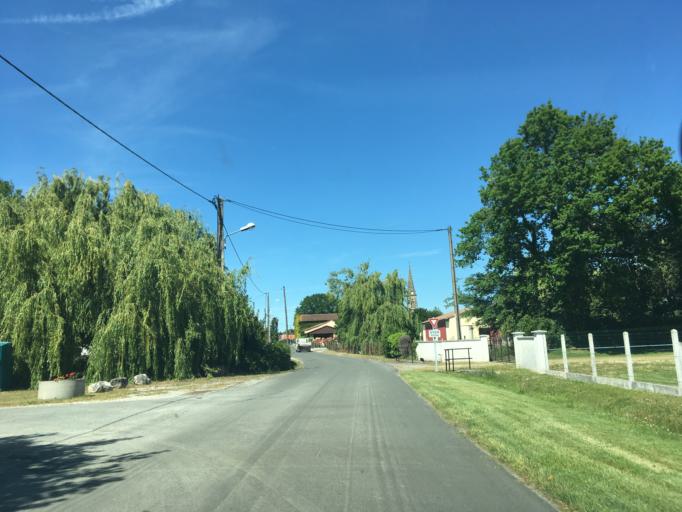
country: FR
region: Aquitaine
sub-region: Departement de la Gironde
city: Lesparre-Medoc
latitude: 45.3210
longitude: -0.8809
